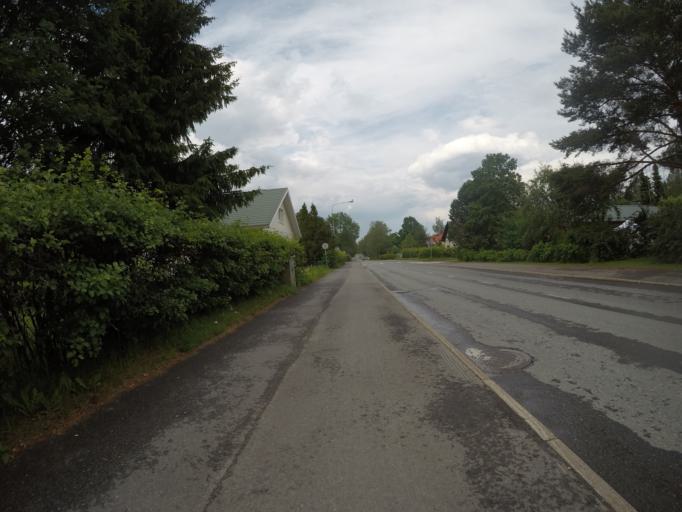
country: FI
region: Haeme
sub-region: Haemeenlinna
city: Haemeenlinna
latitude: 61.0060
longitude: 24.4938
